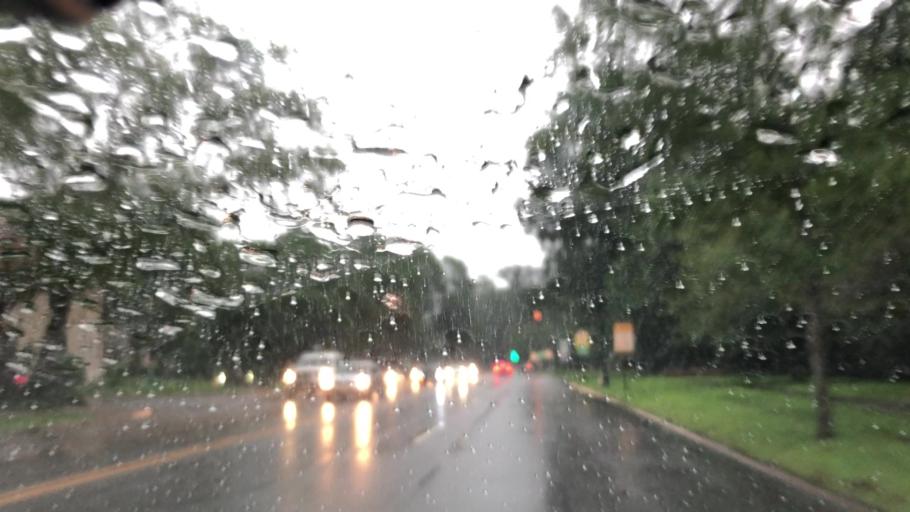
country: US
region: New Jersey
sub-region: Essex County
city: Glen Ridge
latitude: 40.8020
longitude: -74.2053
